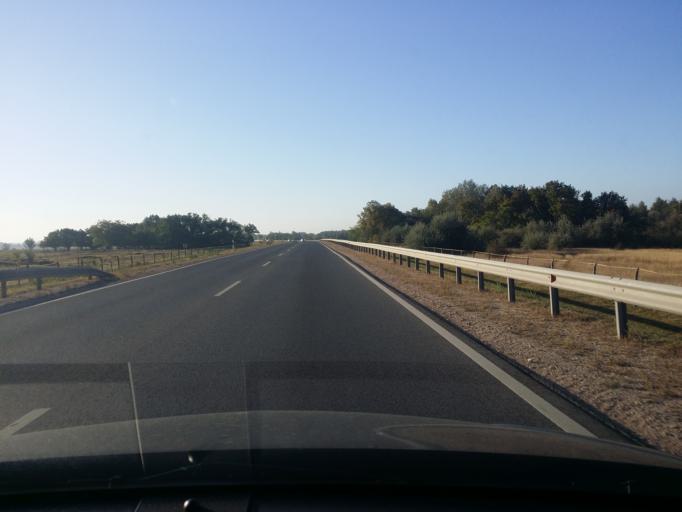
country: HU
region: Bacs-Kiskun
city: Kecskemet
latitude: 46.9334
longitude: 19.7138
